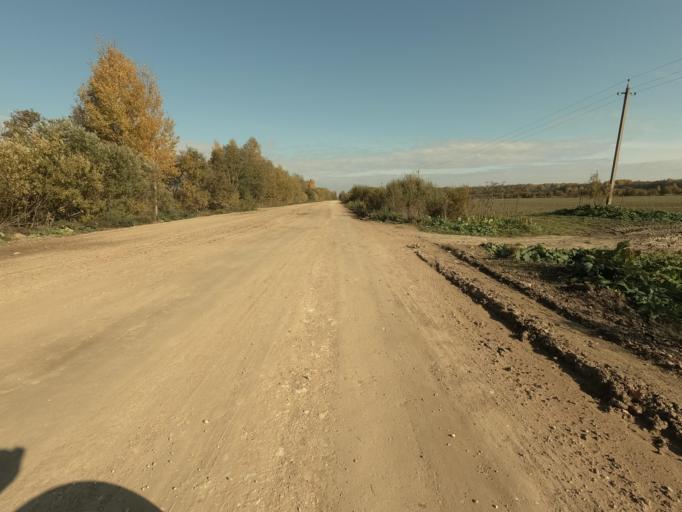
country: RU
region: Novgorod
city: Batetskiy
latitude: 58.8212
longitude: 30.7037
